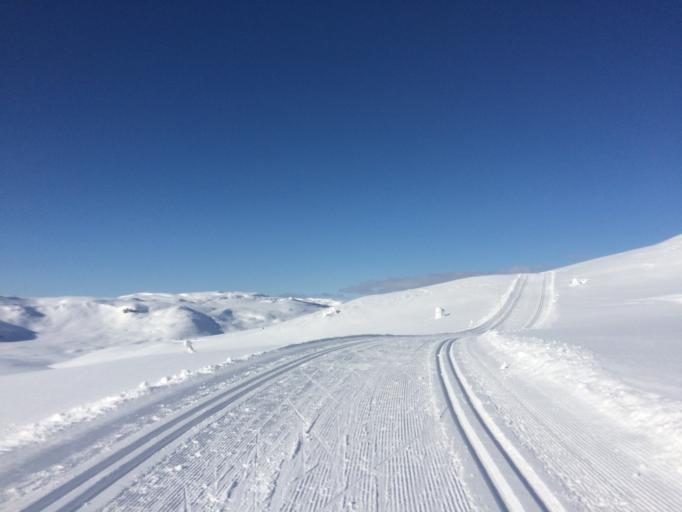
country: NO
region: Oppland
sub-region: Ringebu
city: Ringebu
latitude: 61.3720
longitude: 10.0707
